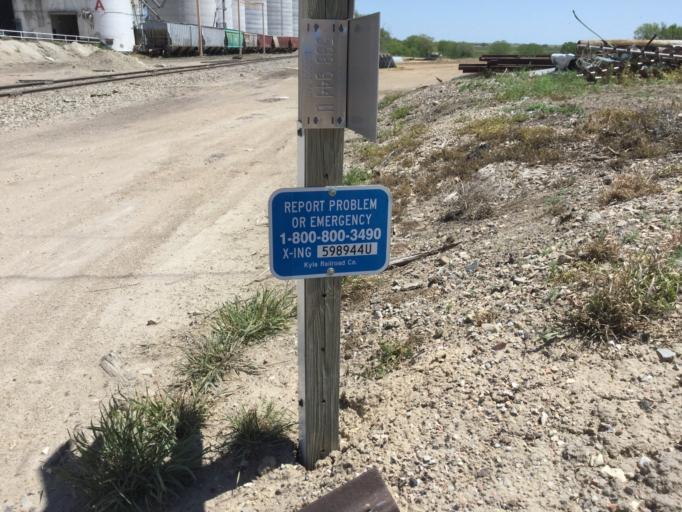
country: US
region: Kansas
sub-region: Smith County
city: Smith Center
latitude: 39.8065
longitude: -98.5552
